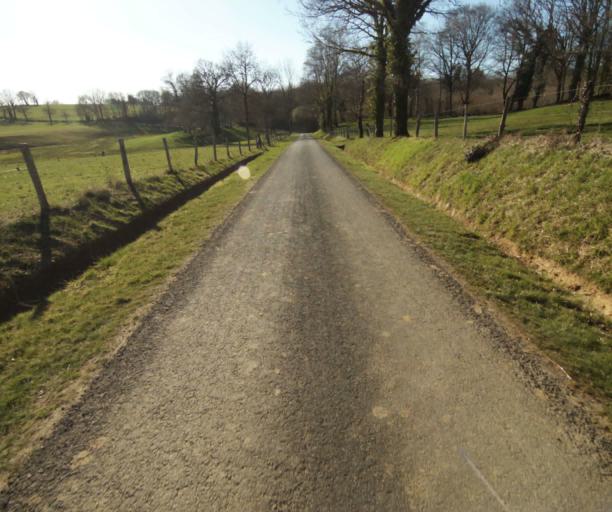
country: FR
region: Limousin
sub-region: Departement de la Correze
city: Seilhac
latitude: 45.3859
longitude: 1.6941
